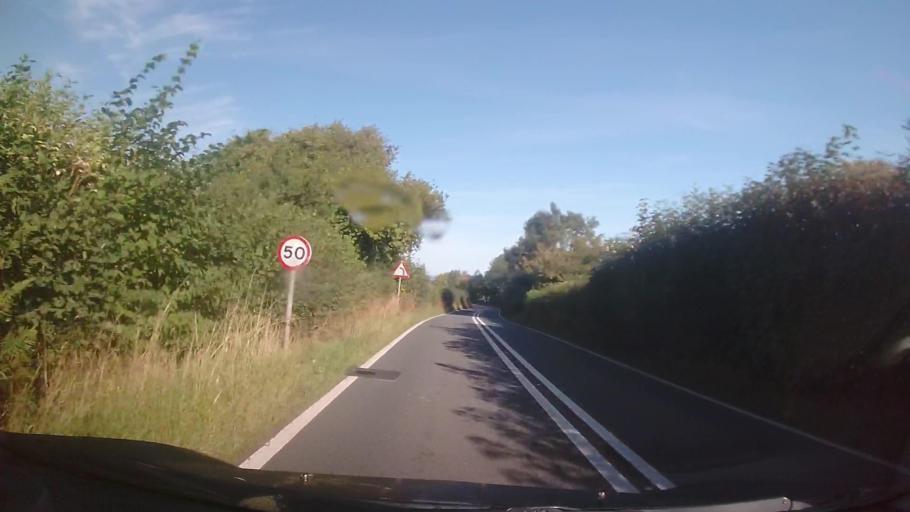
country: GB
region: Wales
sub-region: Sir Powys
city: Hay
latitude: 51.9654
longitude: -3.2096
